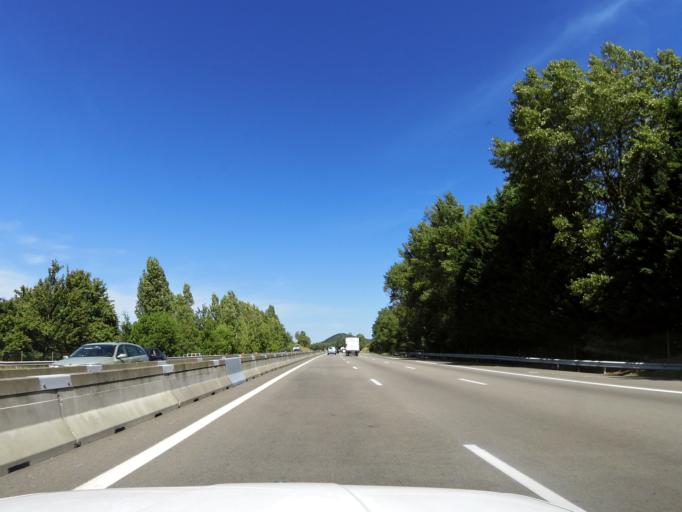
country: FR
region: Rhone-Alpes
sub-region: Departement de la Drome
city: Mercurol
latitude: 45.1132
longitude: 4.8889
